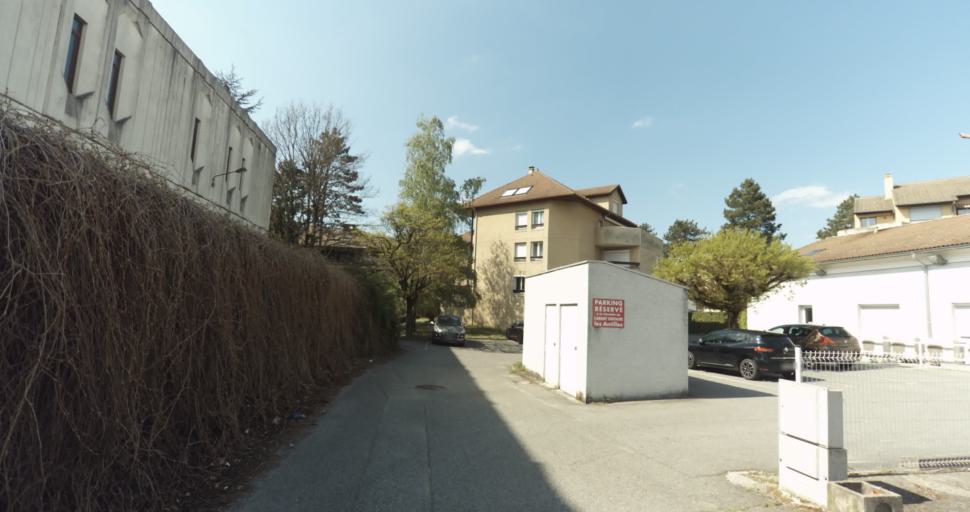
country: FR
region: Rhone-Alpes
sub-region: Departement de l'Isere
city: Saint-Marcellin
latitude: 45.1515
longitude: 5.3162
